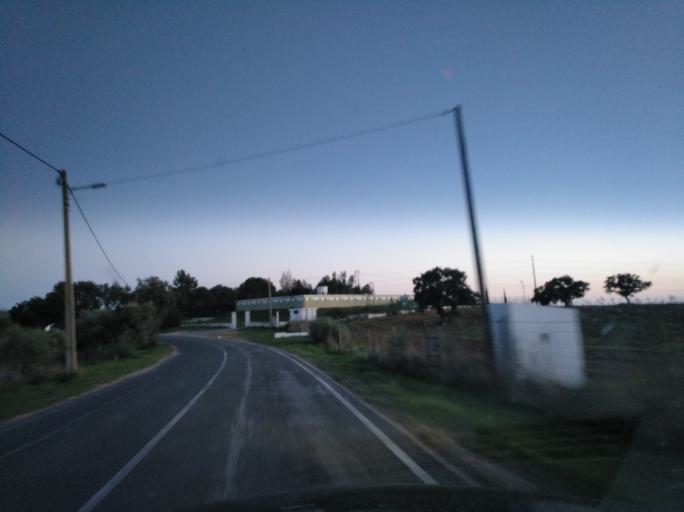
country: PT
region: Faro
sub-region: Vila Real de Santo Antonio
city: Monte Gordo
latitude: 37.1915
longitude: -7.5134
